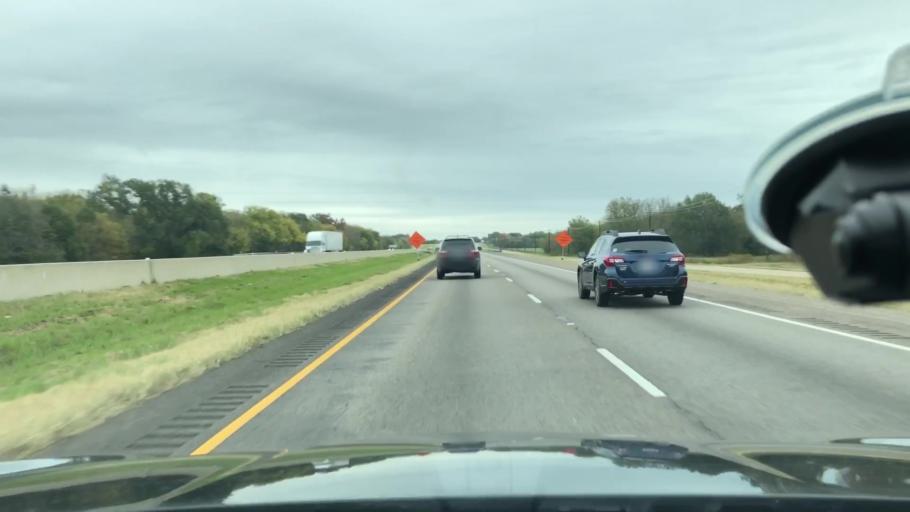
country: US
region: Texas
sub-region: Hopkins County
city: Sulphur Springs
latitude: 33.1490
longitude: -95.4451
